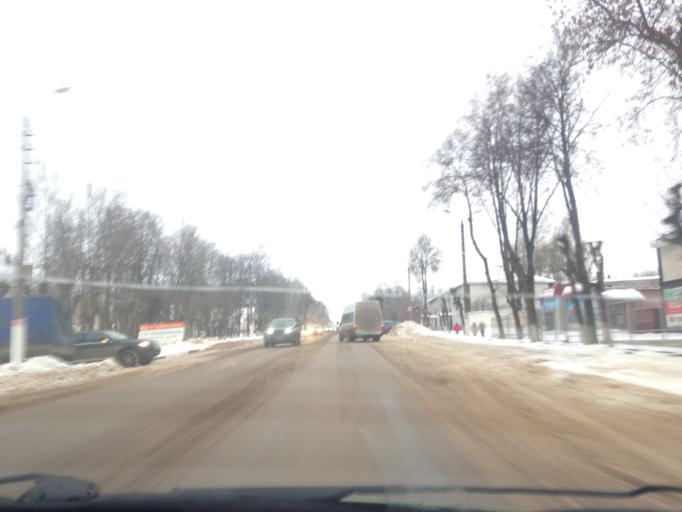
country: RU
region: Tula
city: Shchekino
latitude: 54.0048
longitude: 37.5119
